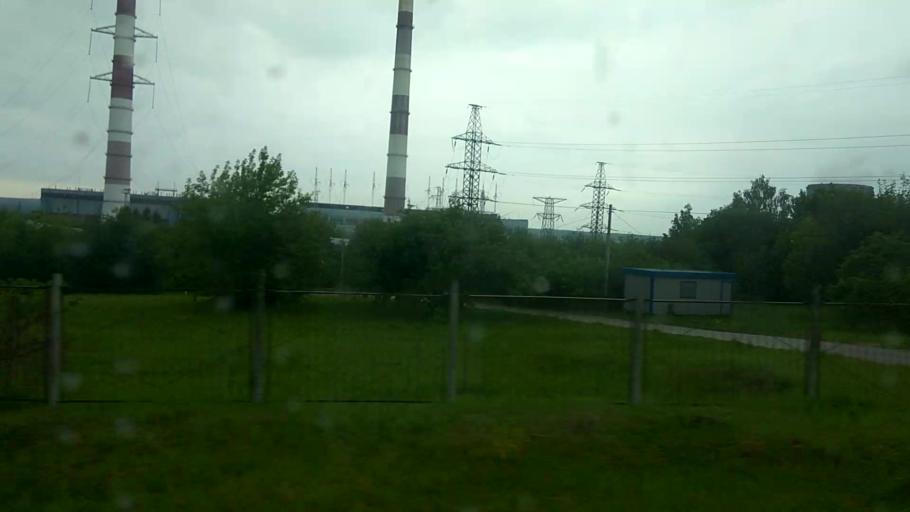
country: RU
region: Moskovskaya
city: Ozherel'ye
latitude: 54.8522
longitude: 38.2589
